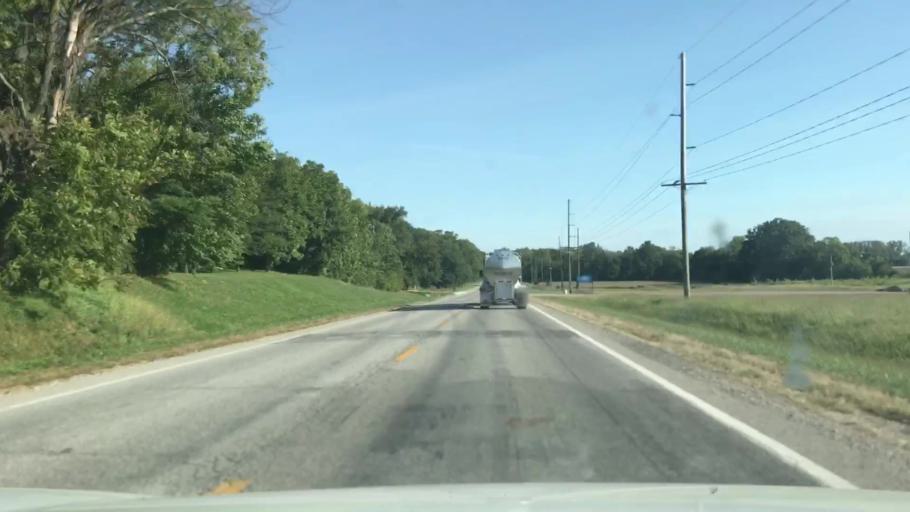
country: US
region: Illinois
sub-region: Adams County
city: Quincy
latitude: 39.8485
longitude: -91.3776
